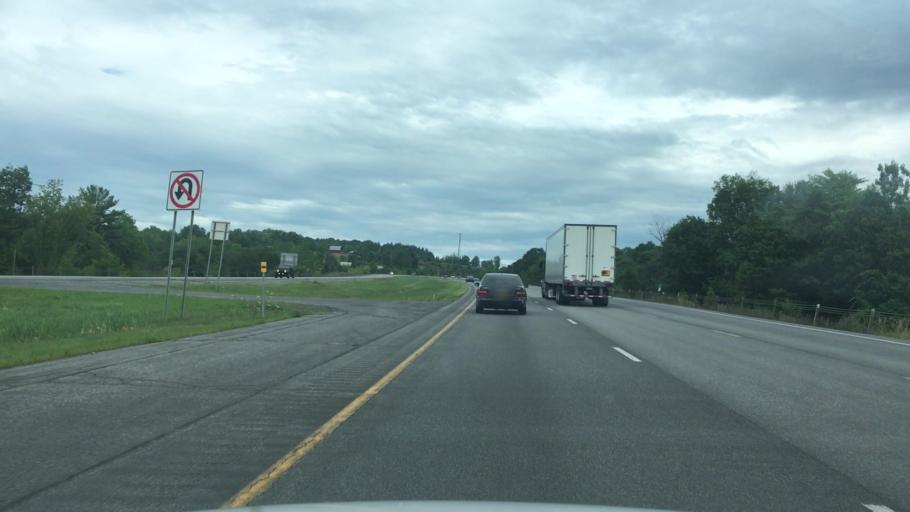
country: US
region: New York
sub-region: Schoharie County
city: Schoharie
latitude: 42.7094
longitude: -74.2994
